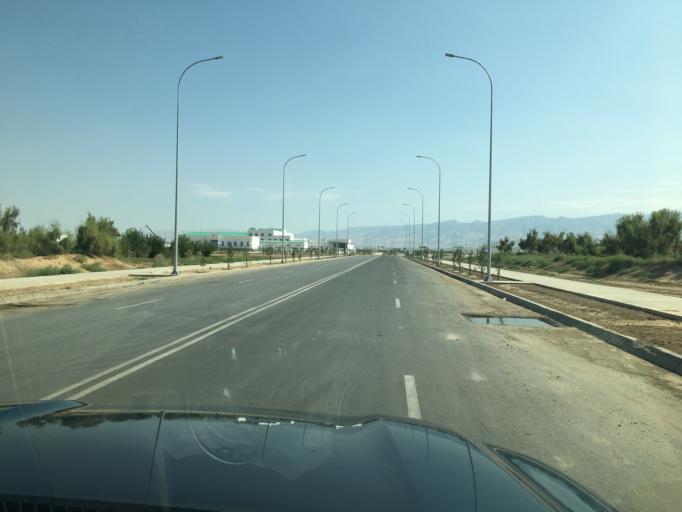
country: TM
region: Ahal
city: Abadan
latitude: 38.1022
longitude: 58.2921
